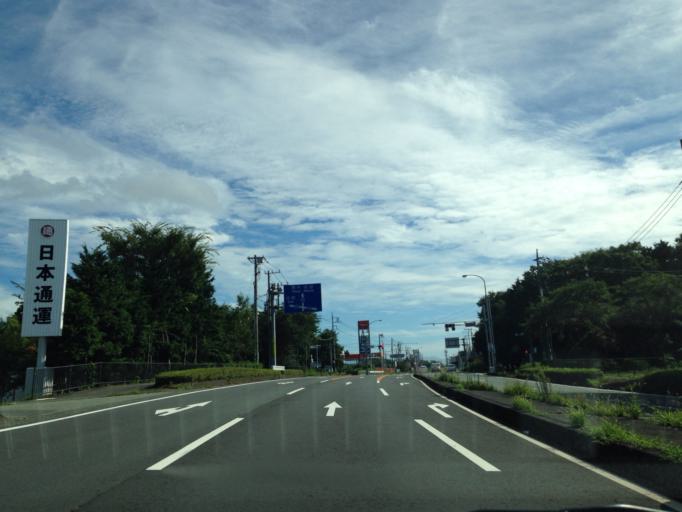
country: JP
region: Shizuoka
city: Gotemba
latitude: 35.2746
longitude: 138.9133
